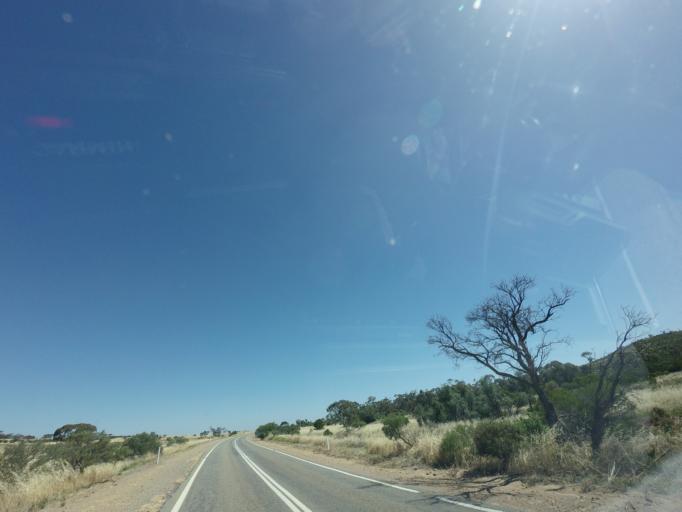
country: AU
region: South Australia
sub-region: Peterborough
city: Peterborough
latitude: -32.9209
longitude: 138.7704
